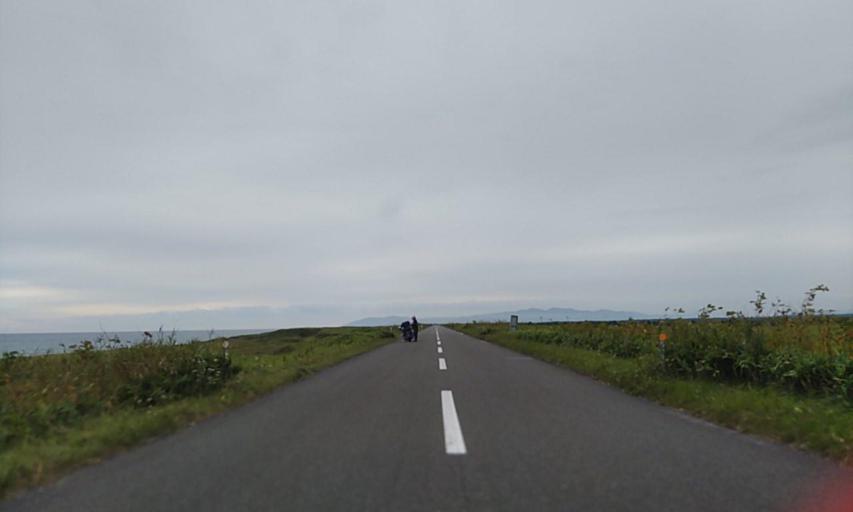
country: JP
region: Hokkaido
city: Makubetsu
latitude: 45.2688
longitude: 142.2384
